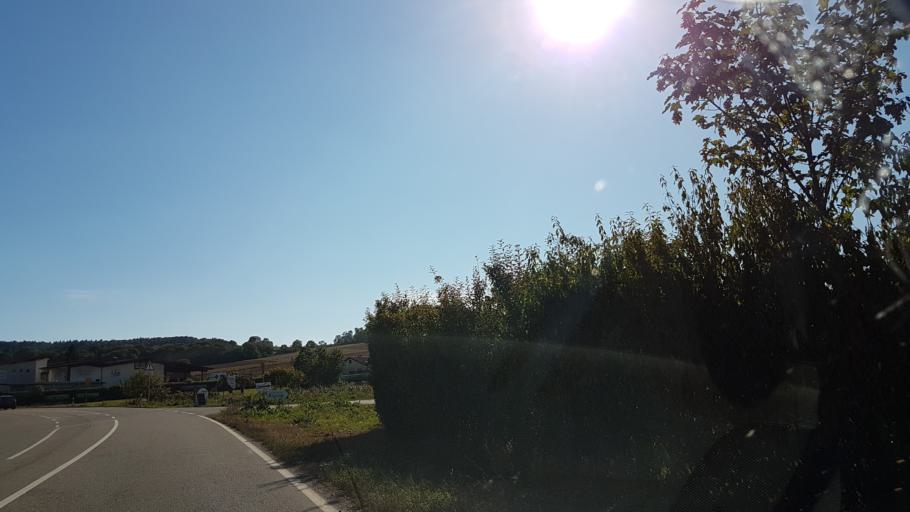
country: DE
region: Baden-Wuerttemberg
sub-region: Regierungsbezirk Stuttgart
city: Erlenbach
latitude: 49.1651
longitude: 9.2641
